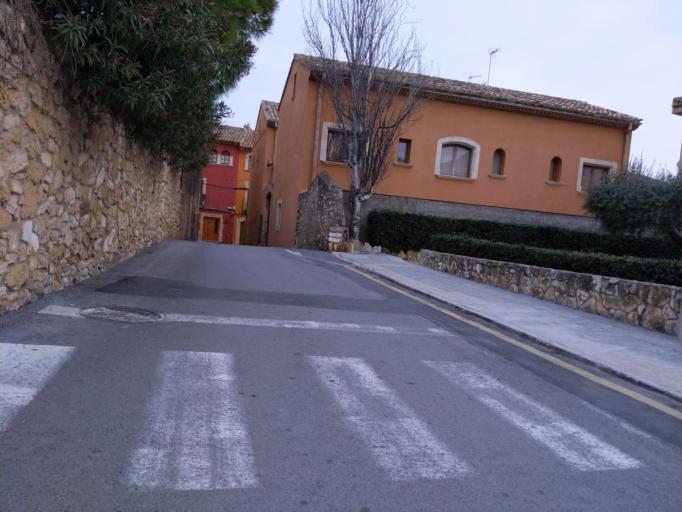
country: ES
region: Catalonia
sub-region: Provincia de Tarragona
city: Altafulla
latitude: 41.1418
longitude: 1.3749
